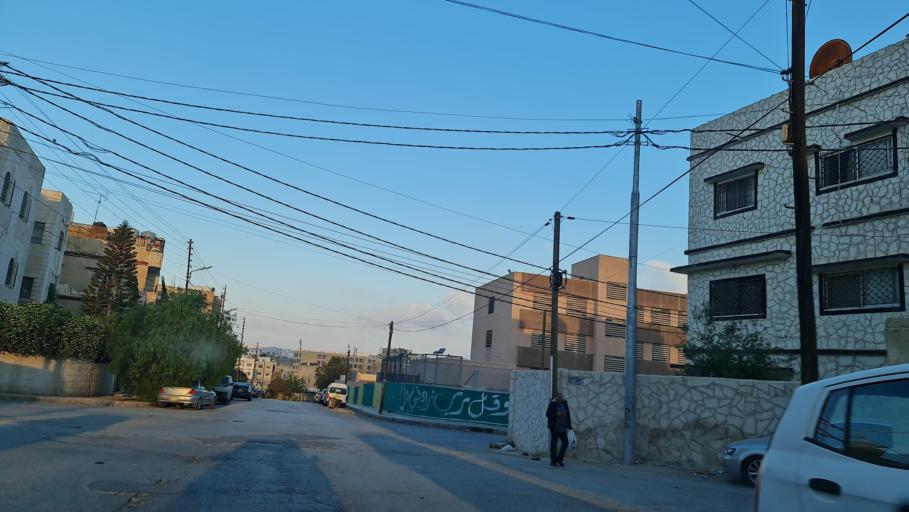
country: JO
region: Zarqa
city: Zarqa
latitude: 32.0753
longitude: 36.0803
